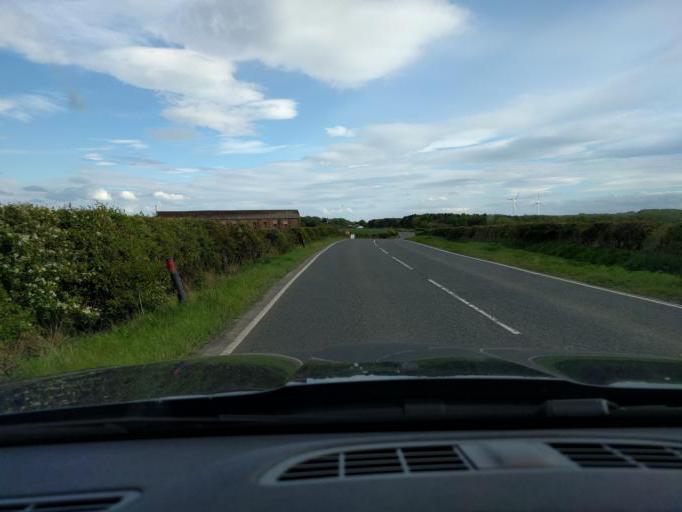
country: GB
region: England
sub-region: Northumberland
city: Bedlington
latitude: 55.1230
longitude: -1.6307
